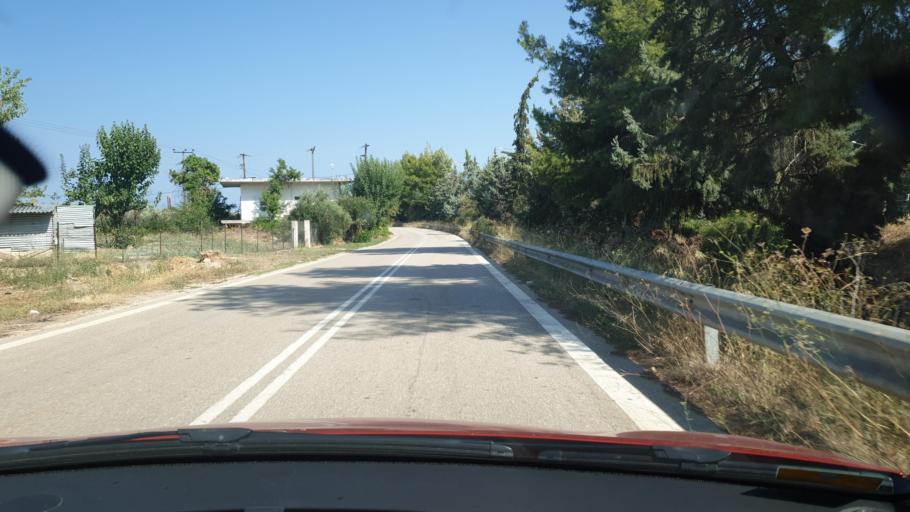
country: GR
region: Central Greece
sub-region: Nomos Fthiotidos
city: Livanates
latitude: 38.7398
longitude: 23.0285
